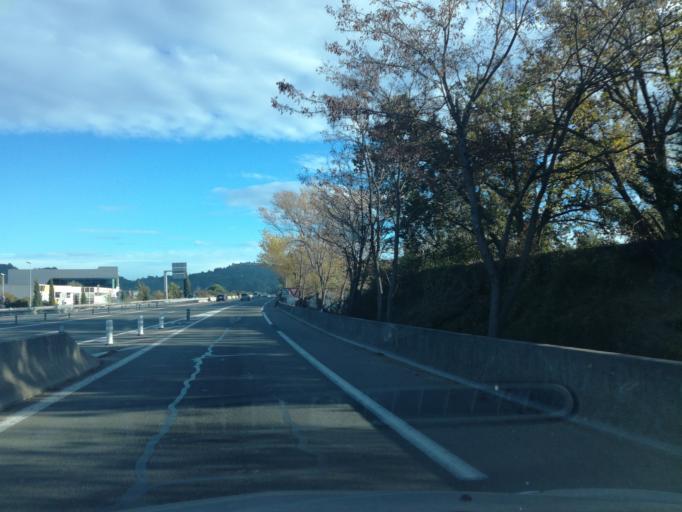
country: FR
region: Provence-Alpes-Cote d'Azur
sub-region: Departement des Alpes-Maritimes
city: Mouans-Sartoux
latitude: 43.6111
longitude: 6.9694
